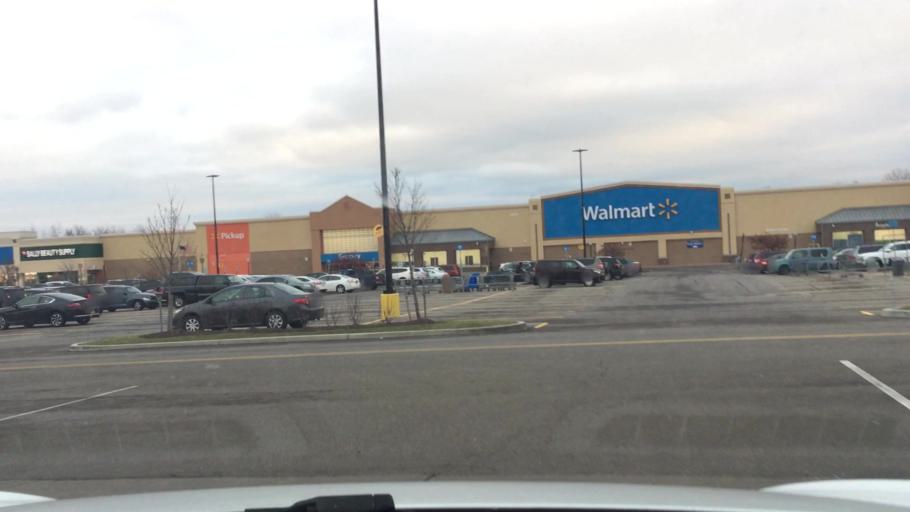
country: US
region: New York
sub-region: Erie County
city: Harris Hill
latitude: 42.9832
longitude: -78.6959
